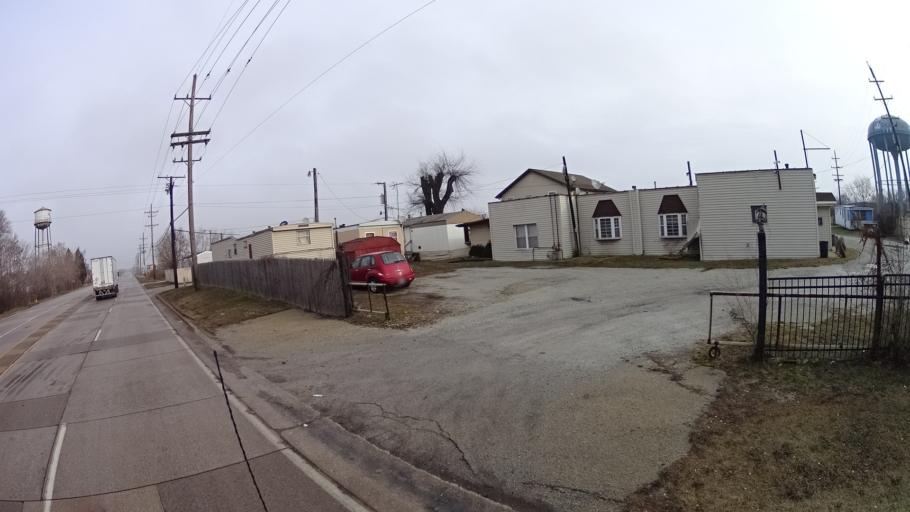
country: US
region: Illinois
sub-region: Cook County
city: Chicago Heights
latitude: 41.5064
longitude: -87.6161
